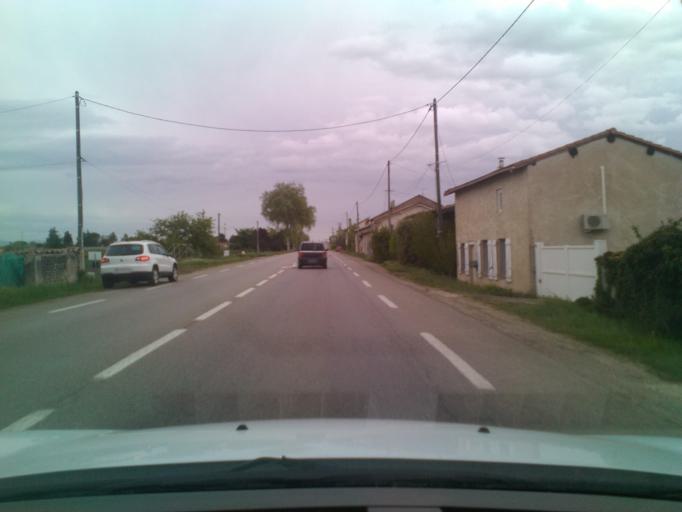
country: FR
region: Rhone-Alpes
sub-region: Departement de la Drome
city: Andancette
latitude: 45.2354
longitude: 4.8190
